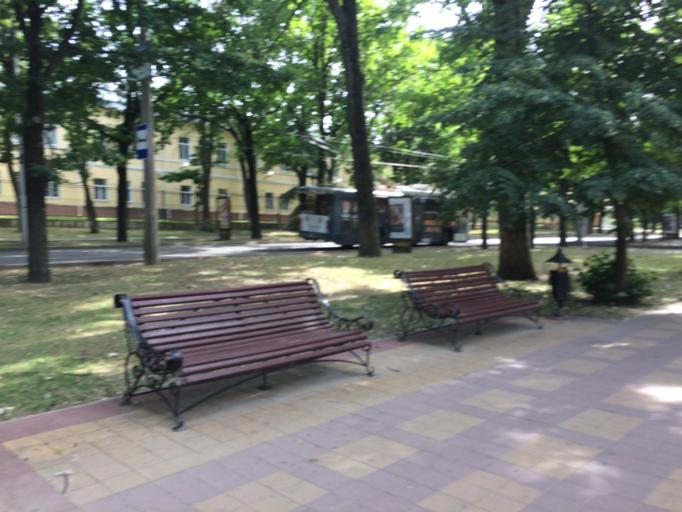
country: RU
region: Stavropol'skiy
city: Stavropol'
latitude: 45.0386
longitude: 41.9563
